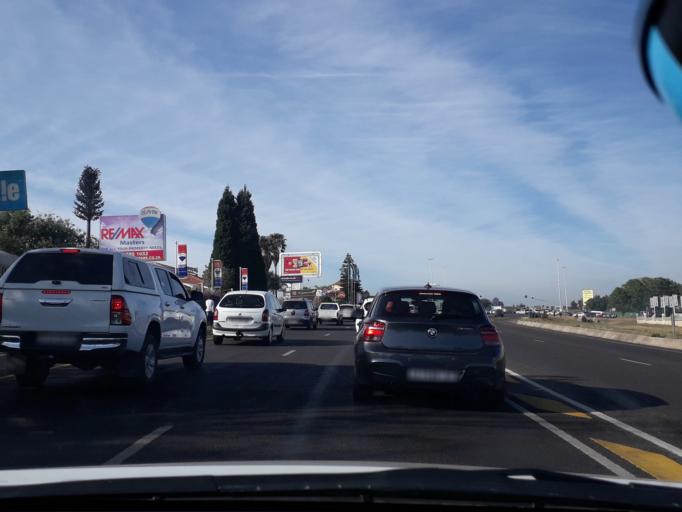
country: ZA
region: Gauteng
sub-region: City of Johannesburg Metropolitan Municipality
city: Roodepoort
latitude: -26.1024
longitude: 27.9262
